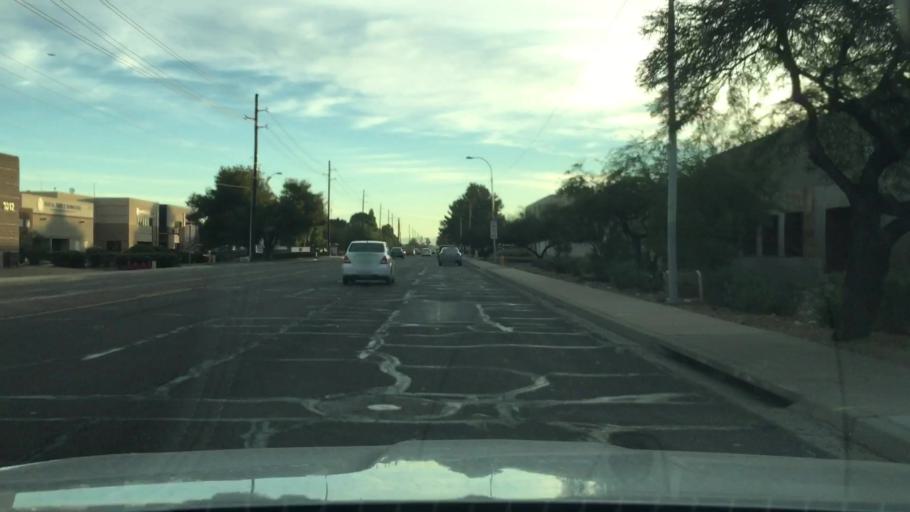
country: US
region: Arizona
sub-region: Maricopa County
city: Guadalupe
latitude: 33.4070
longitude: -112.0104
